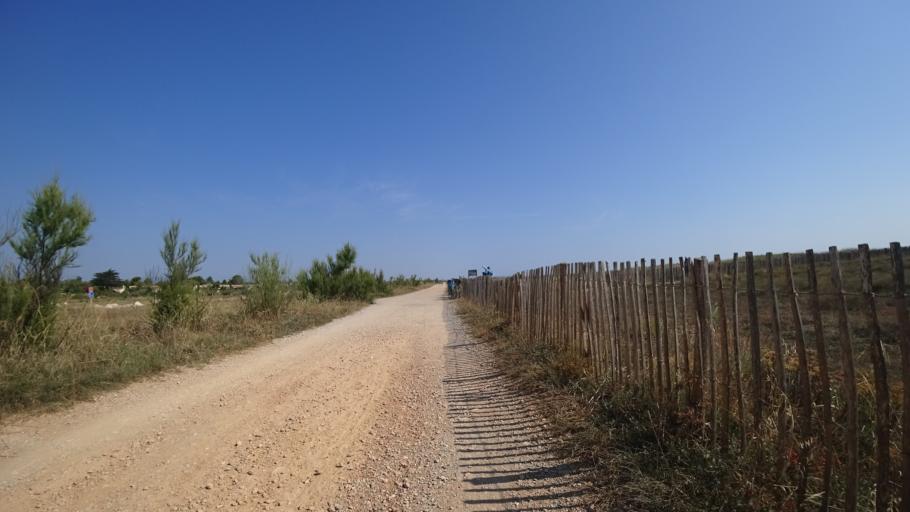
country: FR
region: Languedoc-Roussillon
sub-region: Departement des Pyrenees-Orientales
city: Le Barcares
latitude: 42.7597
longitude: 3.0371
